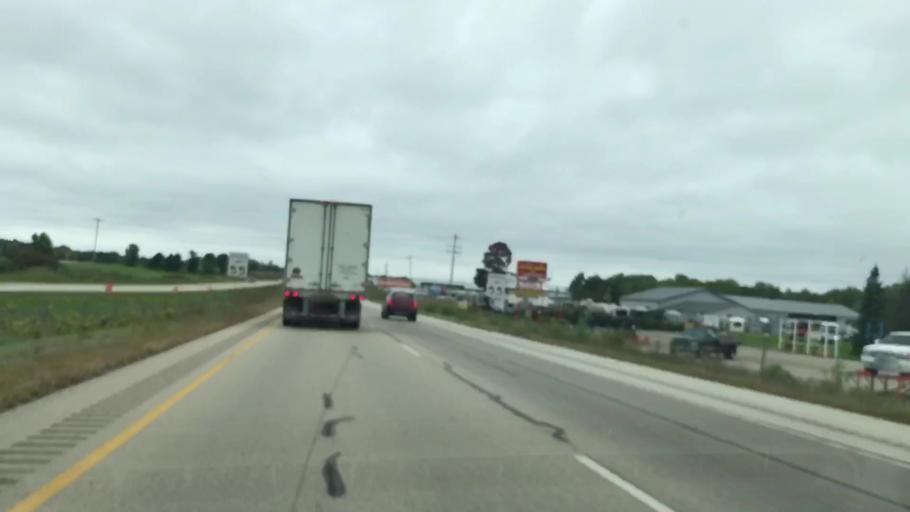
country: US
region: Wisconsin
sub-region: Brown County
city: Suamico
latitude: 44.6695
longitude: -88.0504
